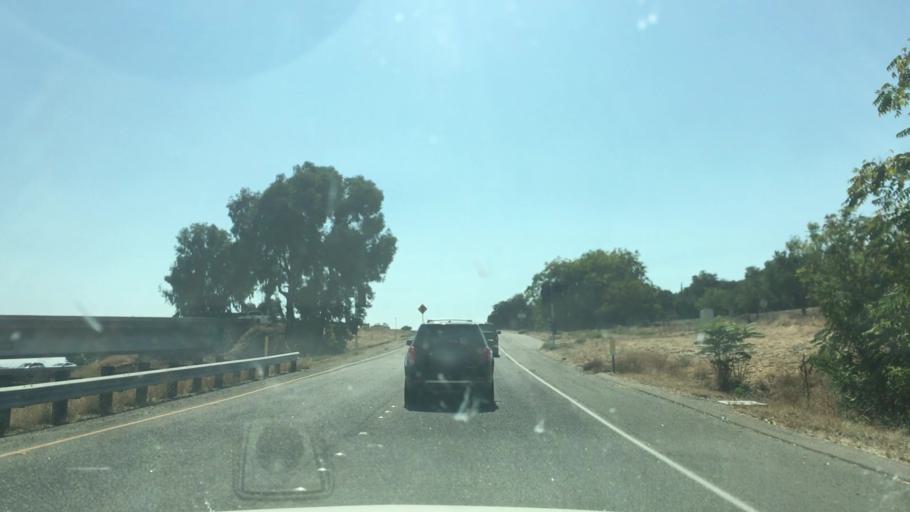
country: US
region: California
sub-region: San Luis Obispo County
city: Paso Robles
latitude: 35.6130
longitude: -120.6911
